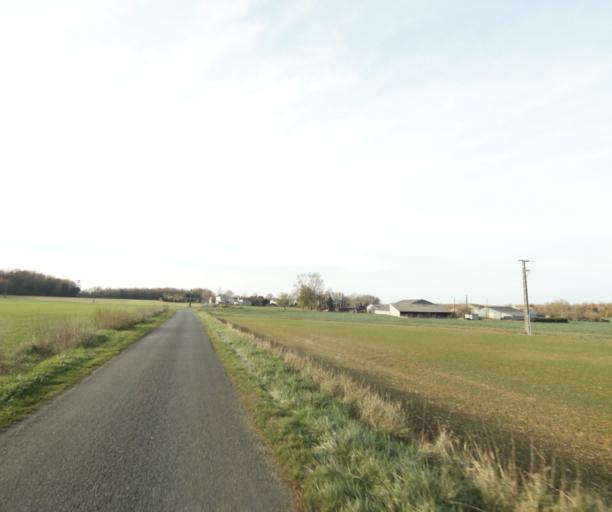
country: FR
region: Poitou-Charentes
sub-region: Departement de la Charente-Maritime
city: Fontcouverte
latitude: 45.8168
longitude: -0.5722
